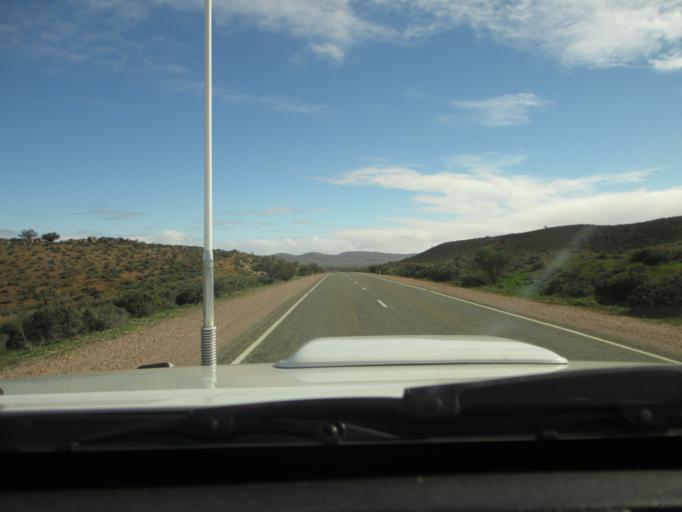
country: AU
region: South Australia
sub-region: Flinders Ranges
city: Quorn
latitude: -31.7836
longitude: 138.3484
